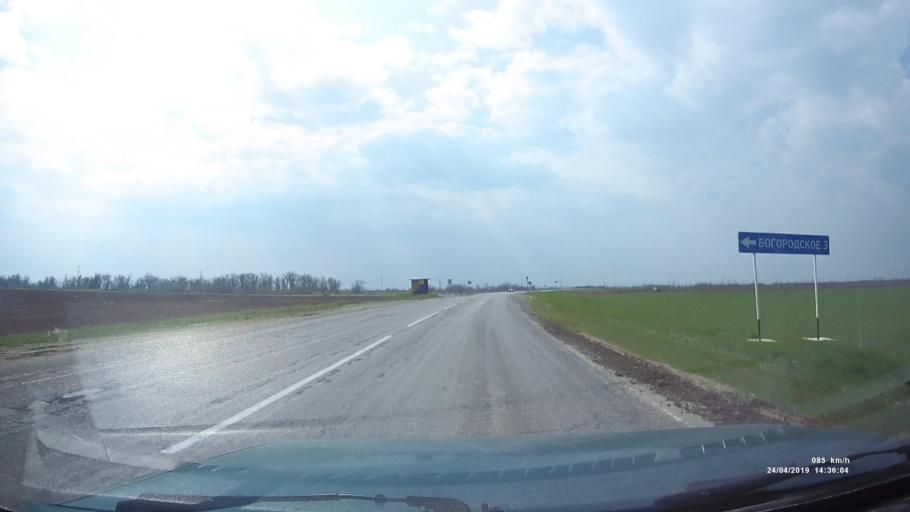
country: RU
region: Rostov
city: Remontnoye
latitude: 46.3756
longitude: 43.8976
